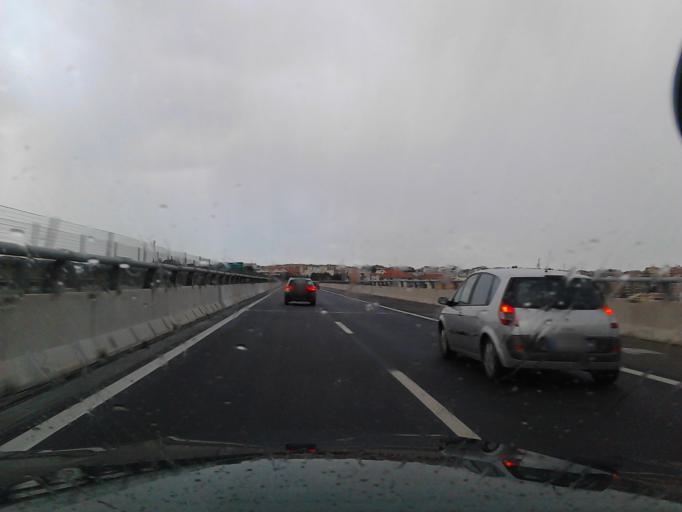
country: IT
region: Molise
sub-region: Provincia di Campobasso
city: Termoli
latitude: 41.9876
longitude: 14.9864
